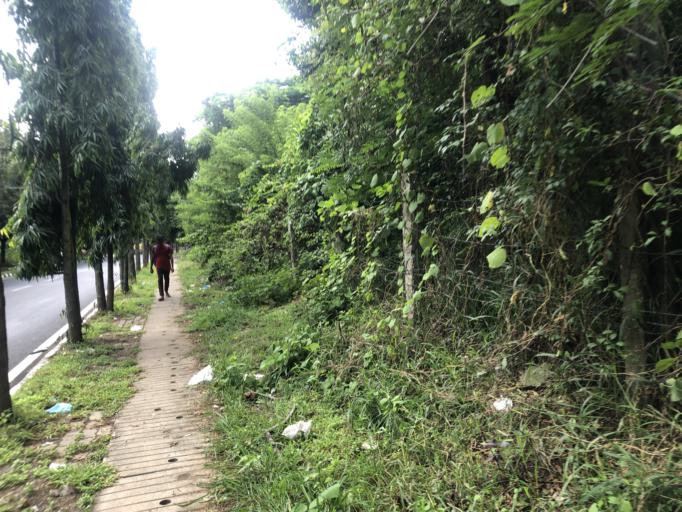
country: IN
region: Karnataka
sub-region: Bangalore Urban
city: Bangalore
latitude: 12.9374
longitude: 77.5108
